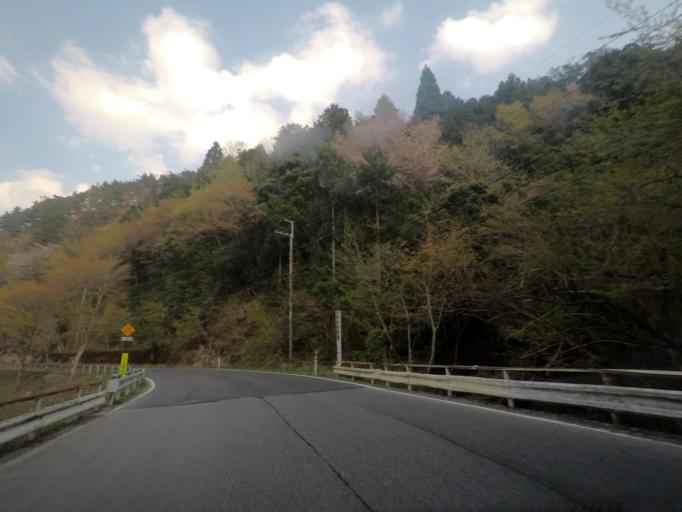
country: JP
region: Shiga Prefecture
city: Hino
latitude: 35.0713
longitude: 136.3431
